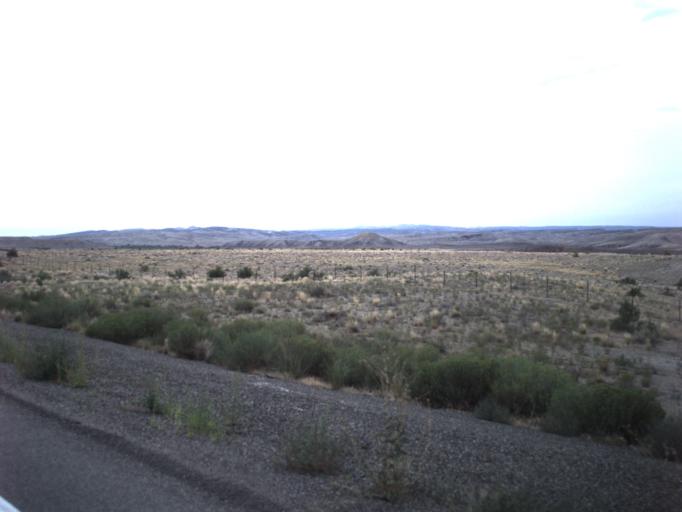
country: US
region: Utah
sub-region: Carbon County
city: East Carbon City
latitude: 39.3307
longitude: -110.3686
